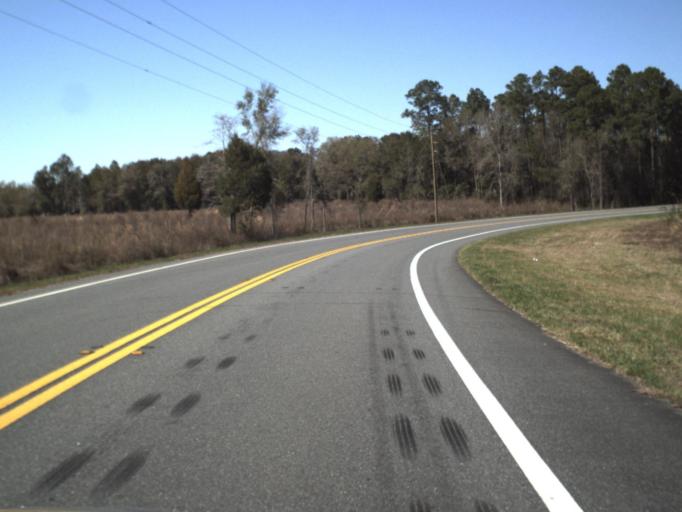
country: US
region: Florida
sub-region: Gulf County
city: Wewahitchka
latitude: 30.2379
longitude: -85.2095
